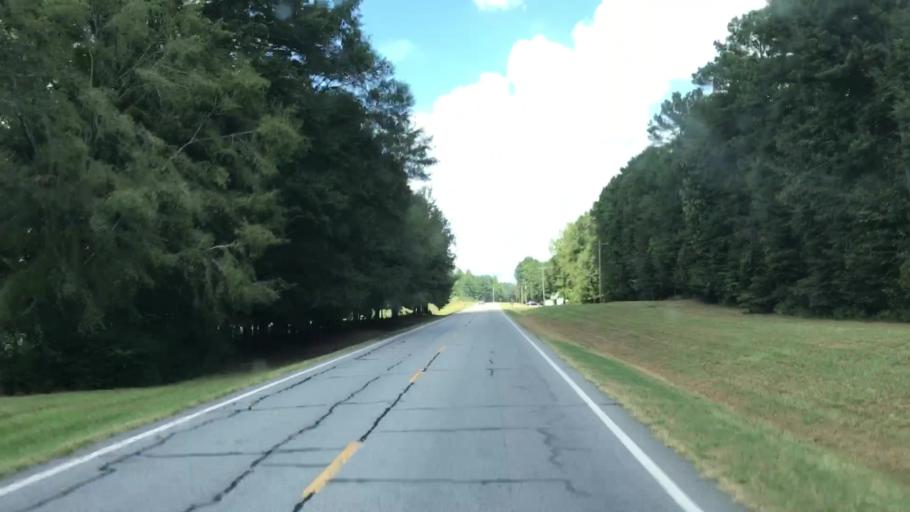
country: US
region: Georgia
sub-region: Oconee County
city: Watkinsville
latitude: 33.7546
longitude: -83.3042
